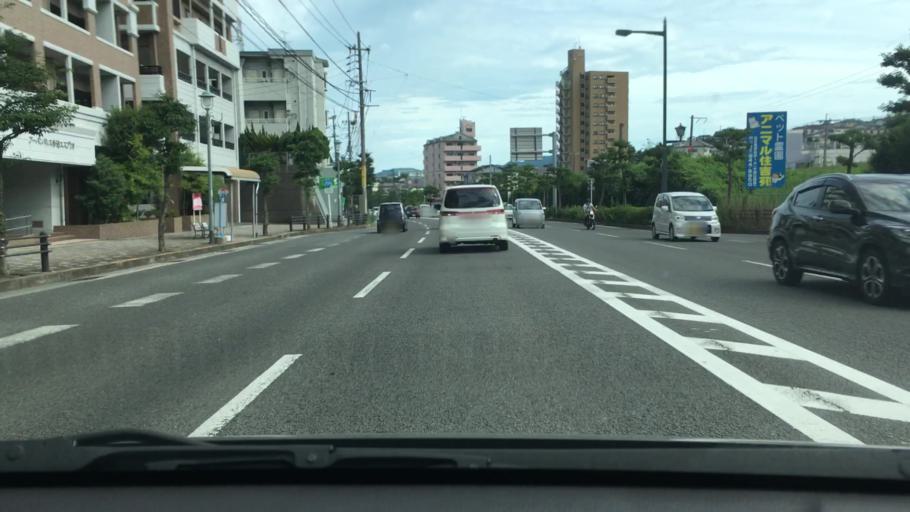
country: JP
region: Nagasaki
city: Obita
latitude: 32.7974
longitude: 129.8545
